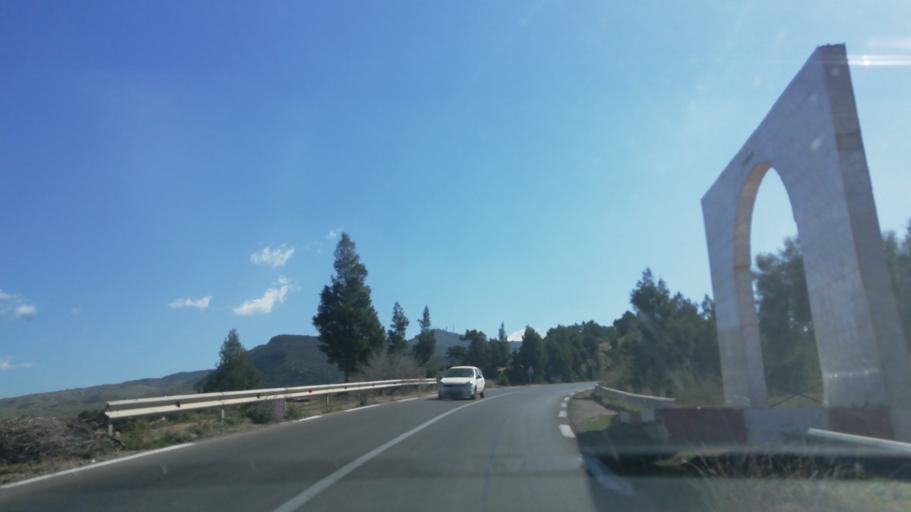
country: DZ
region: Mascara
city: Mascara
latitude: 35.4976
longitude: 0.1327
